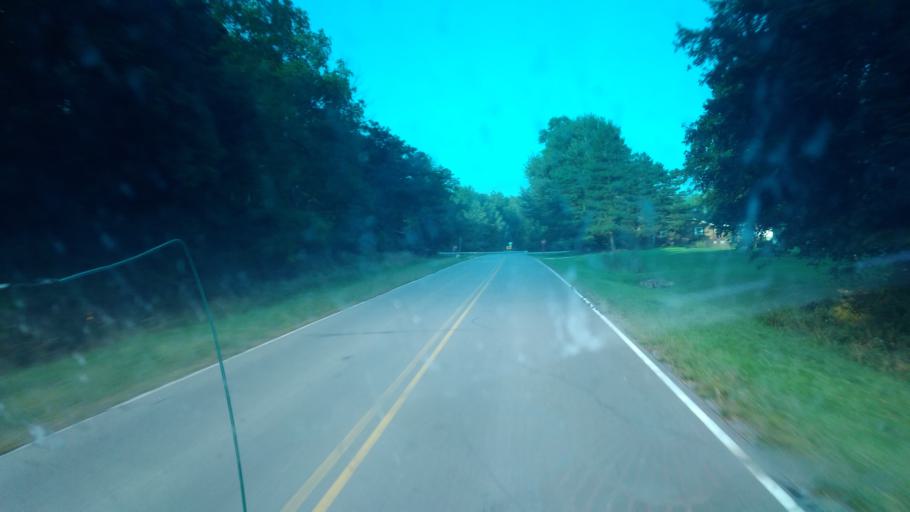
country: US
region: Ohio
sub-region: Crawford County
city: Bucyrus
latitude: 40.8372
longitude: -82.8573
